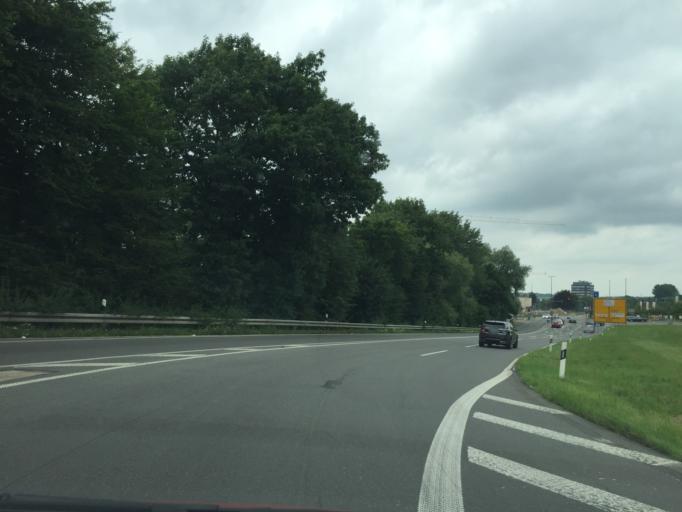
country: DE
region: North Rhine-Westphalia
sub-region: Regierungsbezirk Koln
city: Wurselen
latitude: 50.7545
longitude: 6.1484
